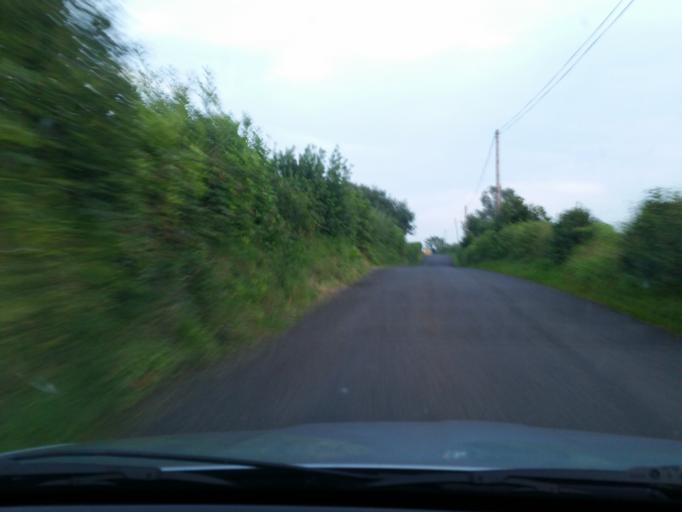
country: GB
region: Northern Ireland
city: Fivemiletown
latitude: 54.3274
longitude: -7.2961
